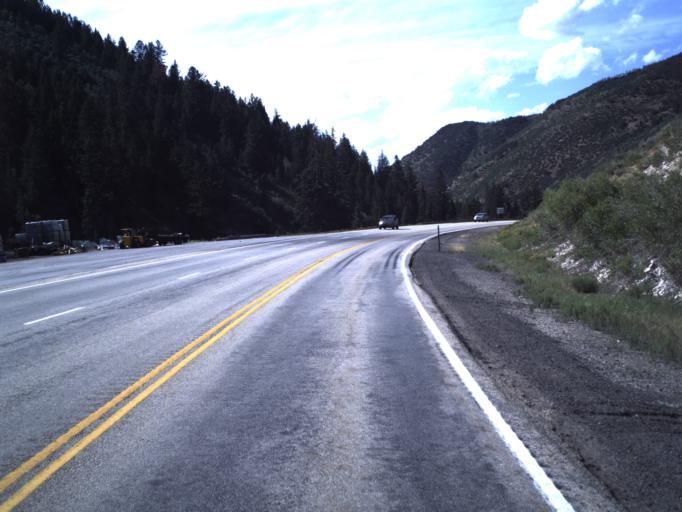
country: US
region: Utah
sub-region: Wasatch County
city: Heber
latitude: 40.3399
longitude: -111.2633
